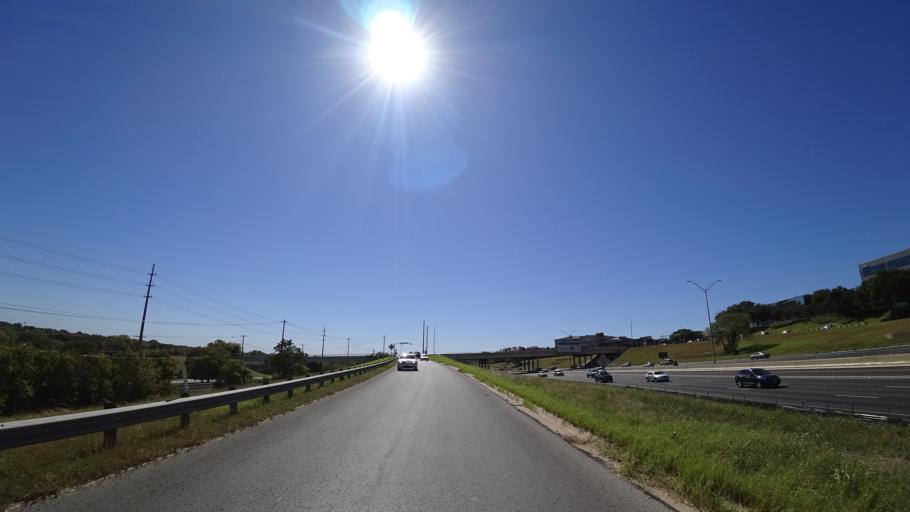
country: US
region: Texas
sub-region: Travis County
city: West Lake Hills
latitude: 30.3529
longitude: -97.7479
